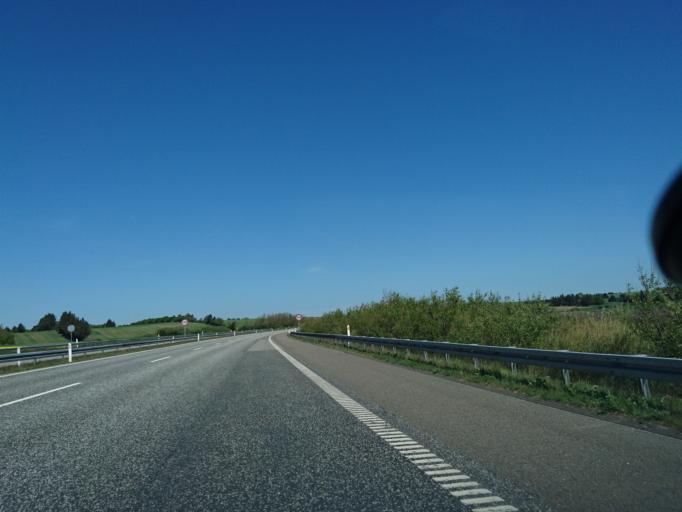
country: DK
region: North Denmark
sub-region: Hjorring Kommune
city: Hjorring
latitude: 57.5170
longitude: 10.0074
